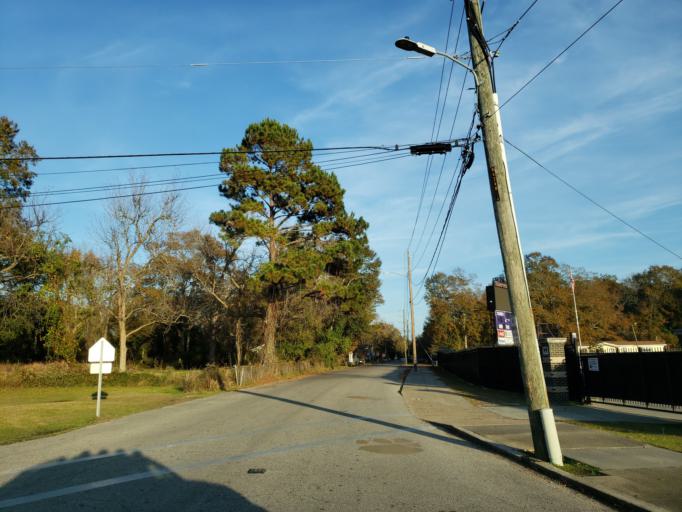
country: US
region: Mississippi
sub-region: Forrest County
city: Hattiesburg
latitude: 31.3302
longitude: -89.3069
